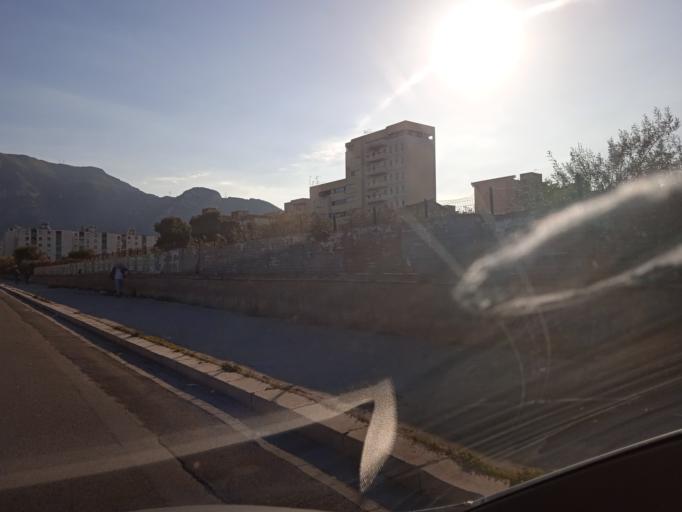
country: IT
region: Sicily
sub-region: Palermo
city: Ciaculli
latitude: 38.0964
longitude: 13.4125
